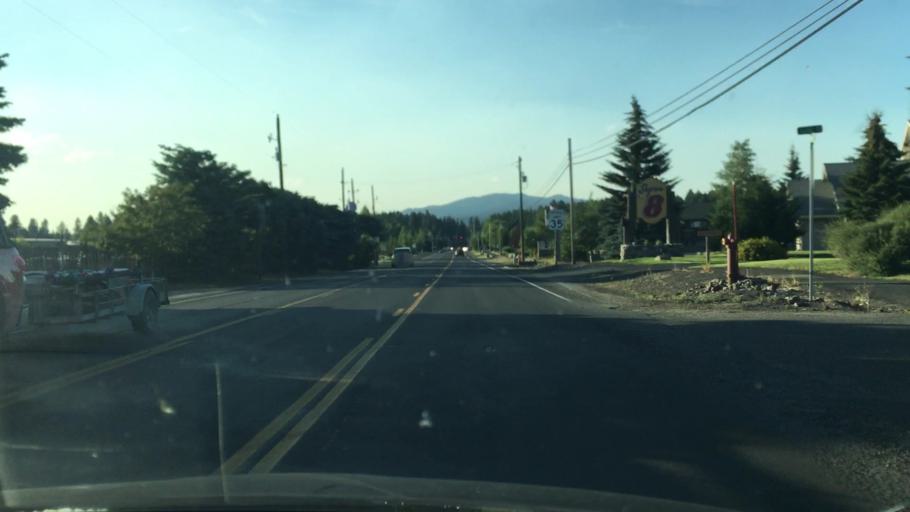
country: US
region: Idaho
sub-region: Valley County
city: McCall
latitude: 44.8941
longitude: -116.0949
